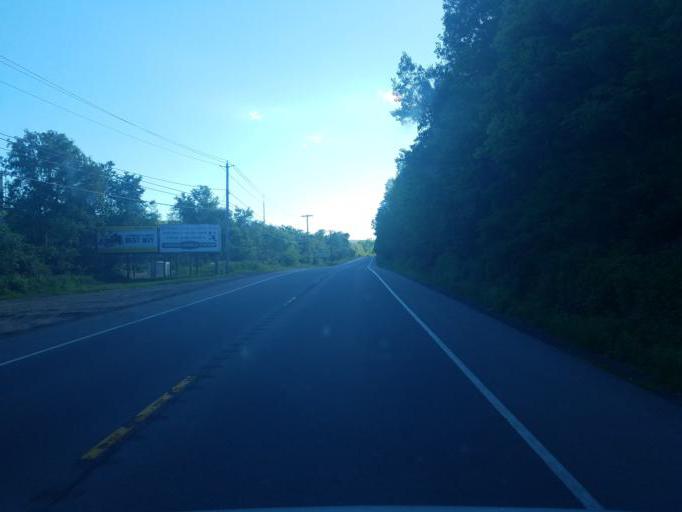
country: US
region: New York
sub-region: Herkimer County
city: Little Falls
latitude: 43.0262
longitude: -74.8842
